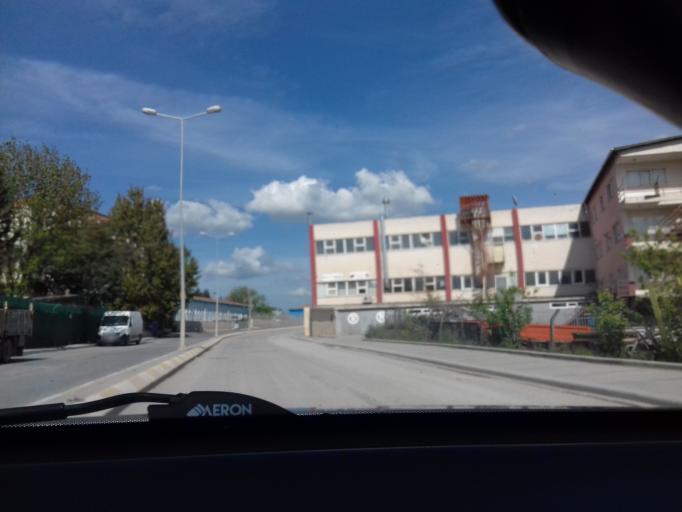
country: TR
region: Istanbul
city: Pendik
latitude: 40.8990
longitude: 29.2836
